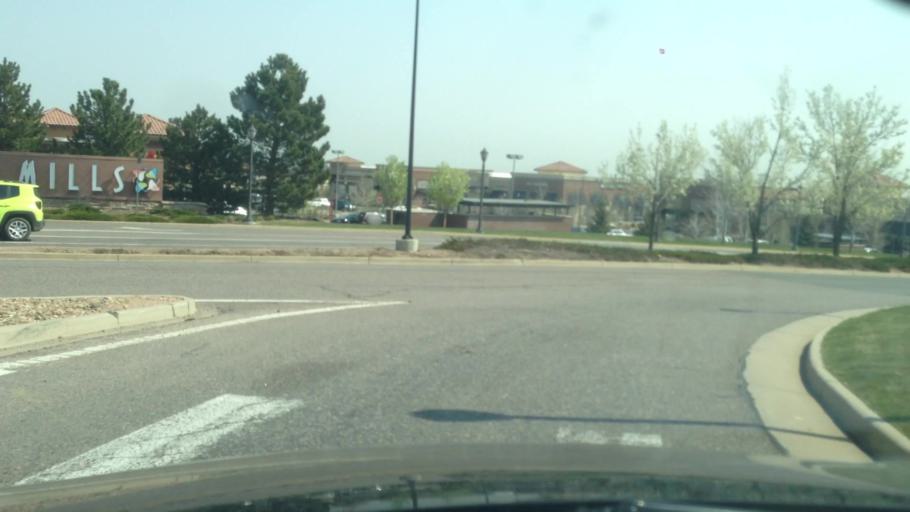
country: US
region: Colorado
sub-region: Jefferson County
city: West Pleasant View
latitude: 39.7295
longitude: -105.1652
